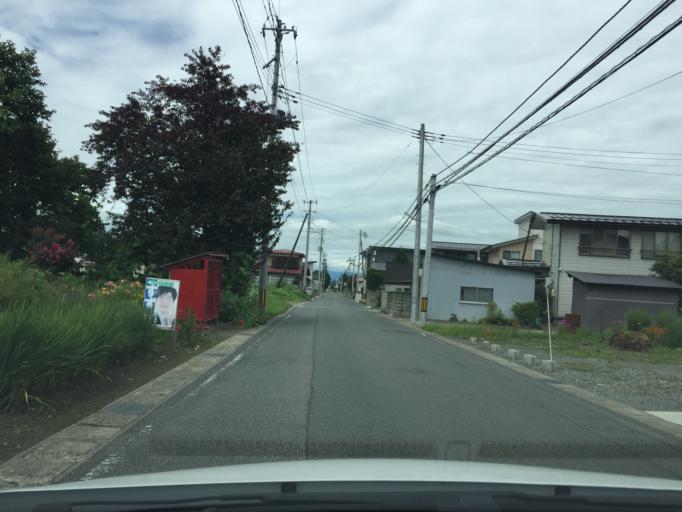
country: JP
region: Yamagata
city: Yonezawa
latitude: 37.8820
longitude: 140.1342
